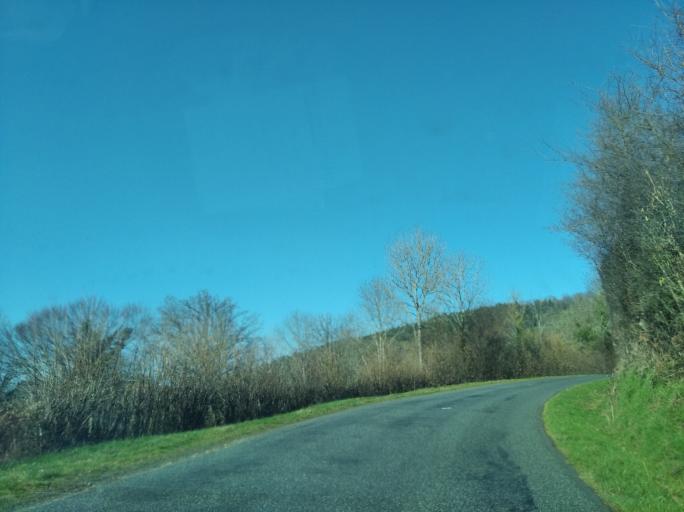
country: FR
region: Auvergne
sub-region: Departement de l'Allier
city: Le Mayet-de-Montagne
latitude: 46.0975
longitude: 3.6786
